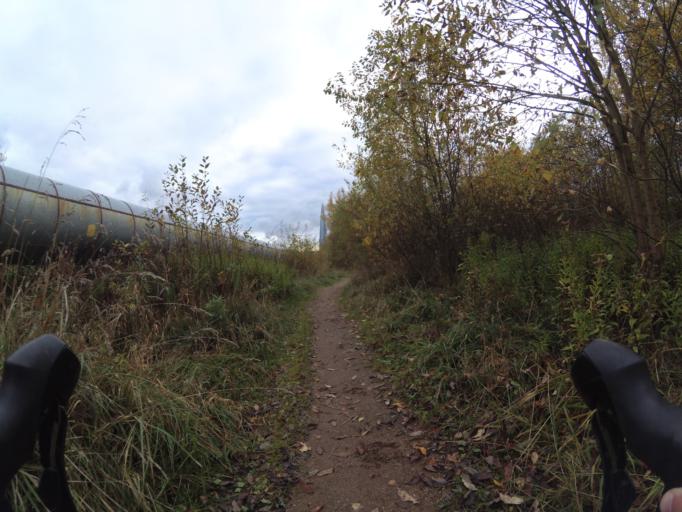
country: RU
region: St.-Petersburg
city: Lakhtinskiy
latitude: 60.0016
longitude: 30.1539
